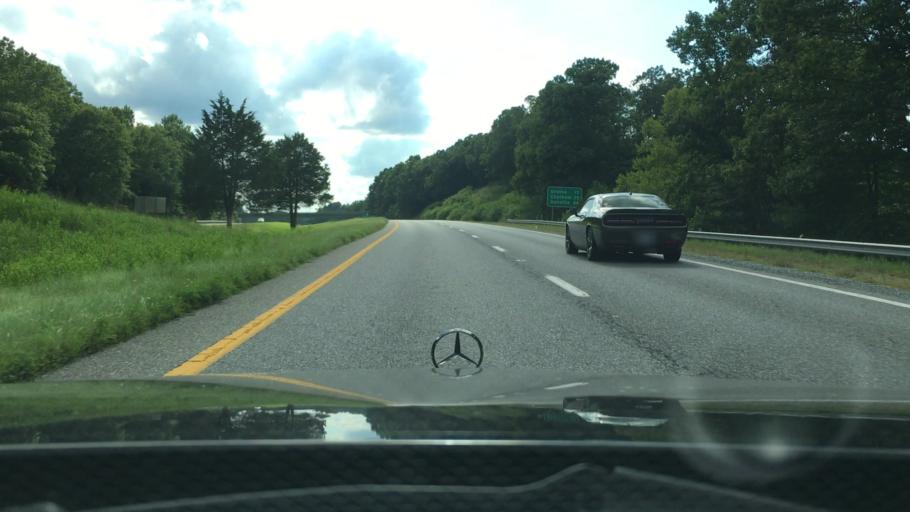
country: US
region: Virginia
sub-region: Campbell County
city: Altavista
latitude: 37.1395
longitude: -79.2629
